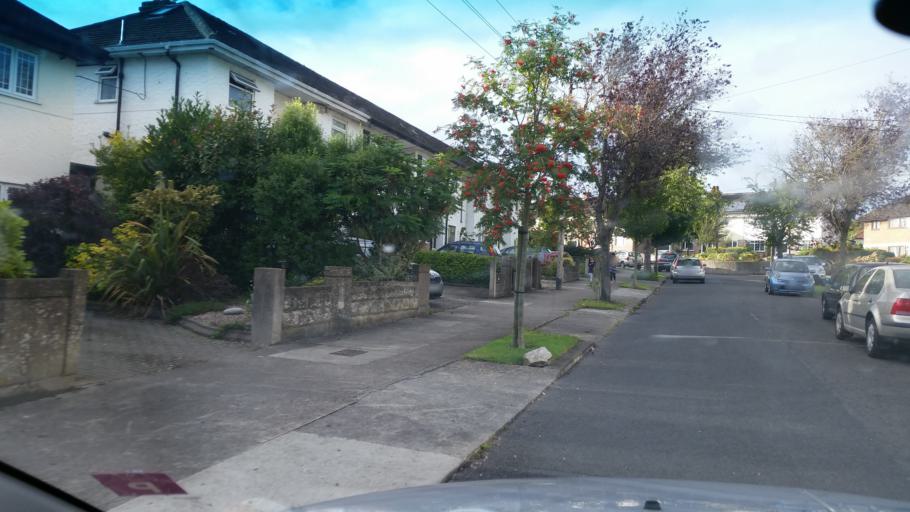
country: IE
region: Leinster
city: Glasnevin
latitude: 53.3796
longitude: -6.2626
